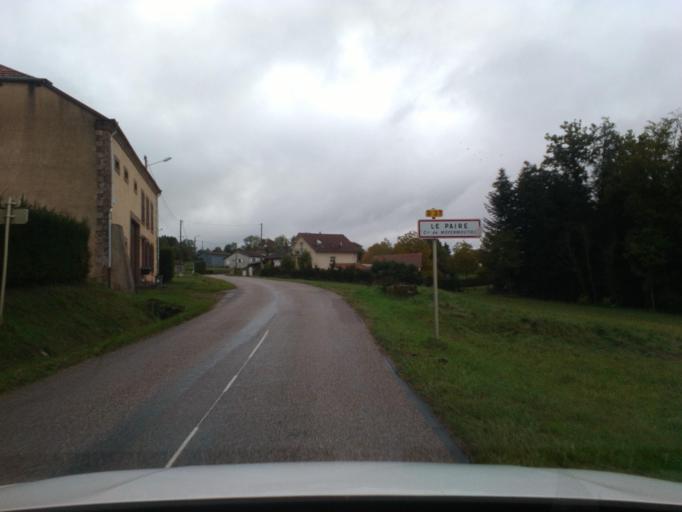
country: FR
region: Lorraine
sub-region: Departement des Vosges
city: Moyenmoutier
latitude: 48.3700
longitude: 6.9266
